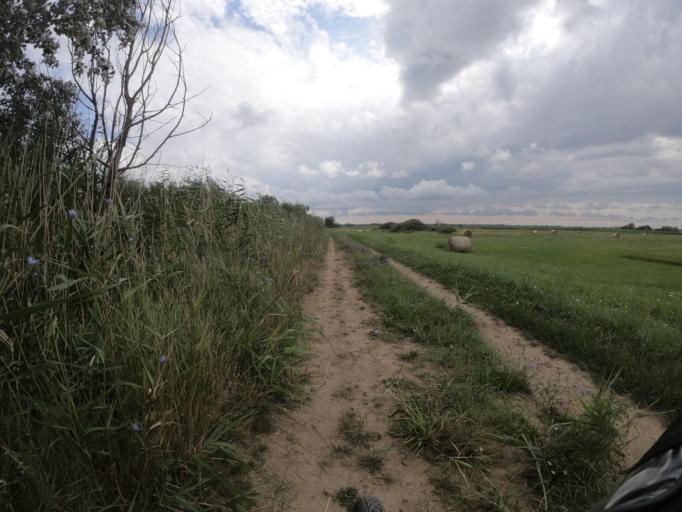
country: HU
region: Jasz-Nagykun-Szolnok
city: Tiszafured
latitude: 47.7085
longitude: 20.7777
